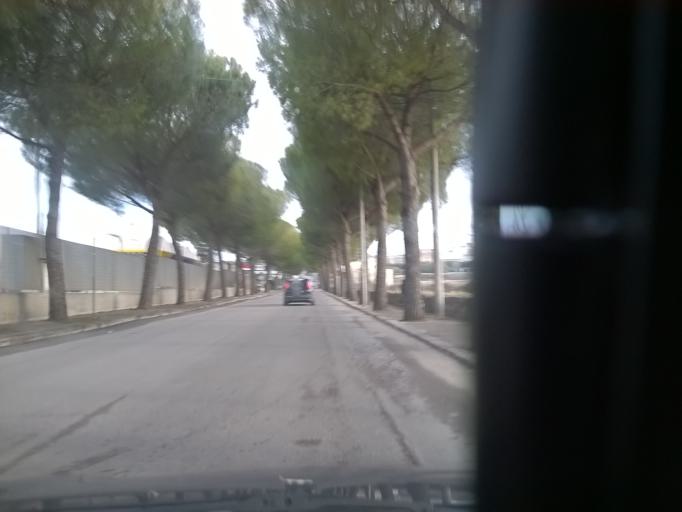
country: IT
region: Apulia
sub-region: Provincia di Taranto
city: Grottaglie
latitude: 40.5312
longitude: 17.4236
